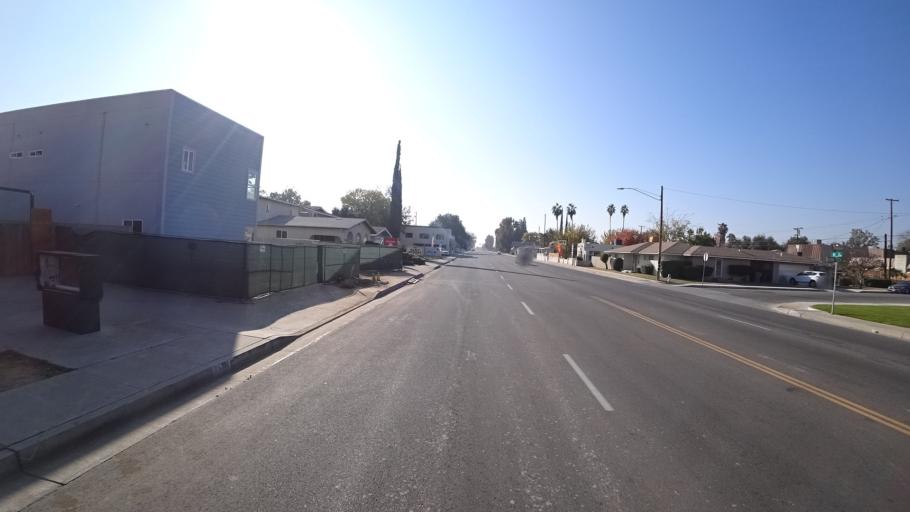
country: US
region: California
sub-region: Kern County
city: Bakersfield
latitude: 35.3601
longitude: -119.0213
